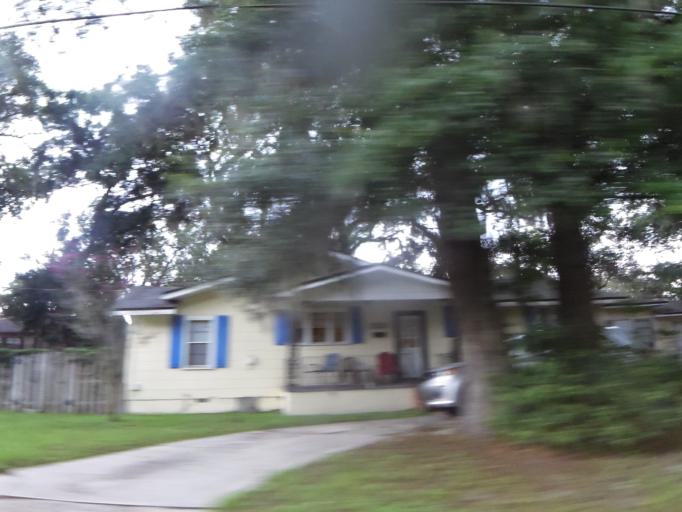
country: US
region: Florida
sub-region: Duval County
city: Jacksonville
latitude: 30.3450
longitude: -81.6063
